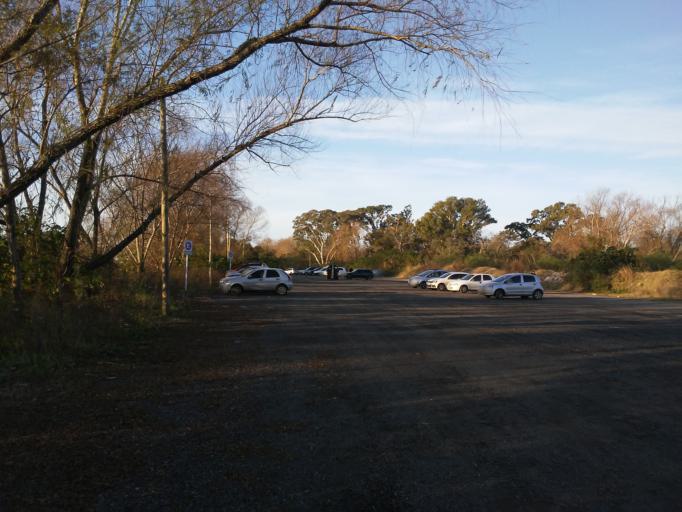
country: AR
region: Buenos Aires
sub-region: Partido de Avellaneda
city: Avellaneda
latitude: -34.6643
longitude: -58.3221
